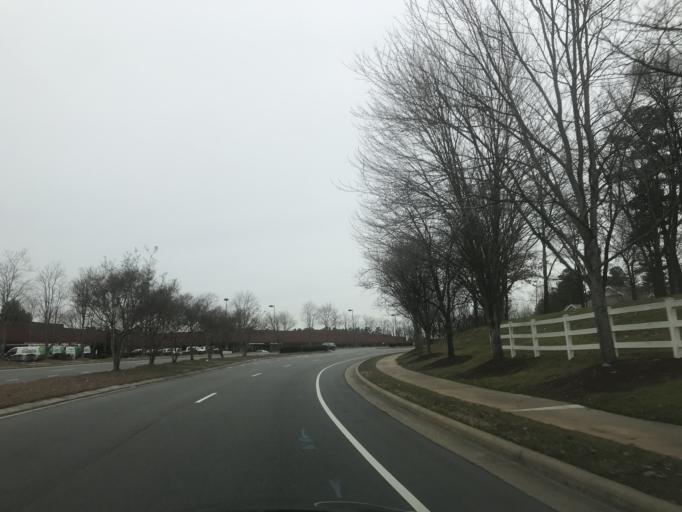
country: US
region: North Carolina
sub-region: Wake County
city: Raleigh
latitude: 35.8692
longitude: -78.5896
